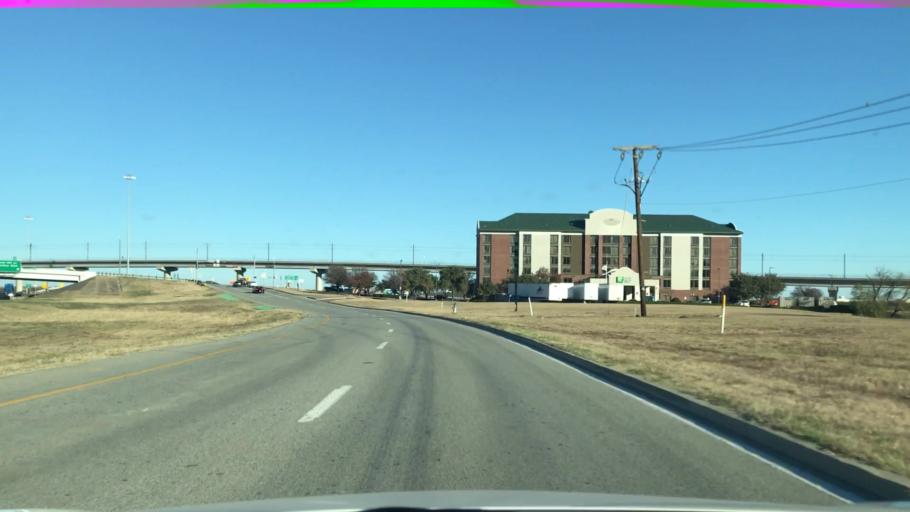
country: US
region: Texas
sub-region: Dallas County
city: Irving
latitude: 32.8777
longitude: -96.9459
